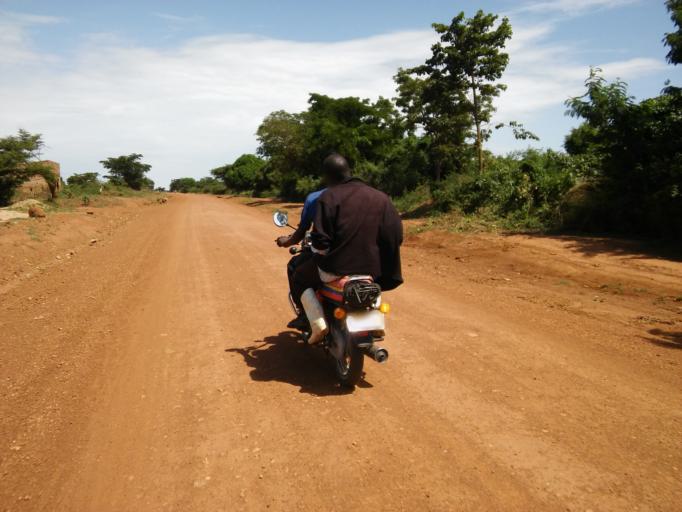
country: UG
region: Eastern Region
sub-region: Kumi District
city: Kumi
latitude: 1.4798
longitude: 33.8928
